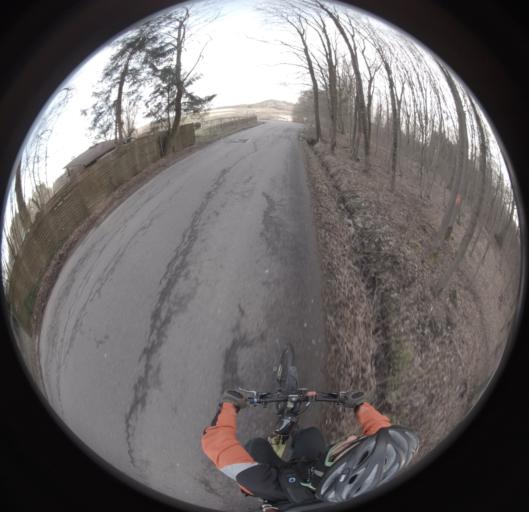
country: DE
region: Baden-Wuerttemberg
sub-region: Regierungsbezirk Stuttgart
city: Birenbach
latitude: 48.7213
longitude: 9.6779
